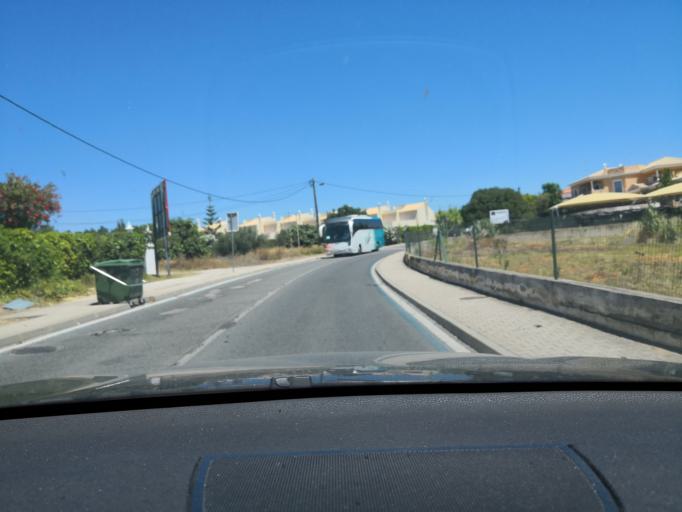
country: PT
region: Faro
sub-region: Albufeira
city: Ferreiras
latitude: 37.1008
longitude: -8.2167
